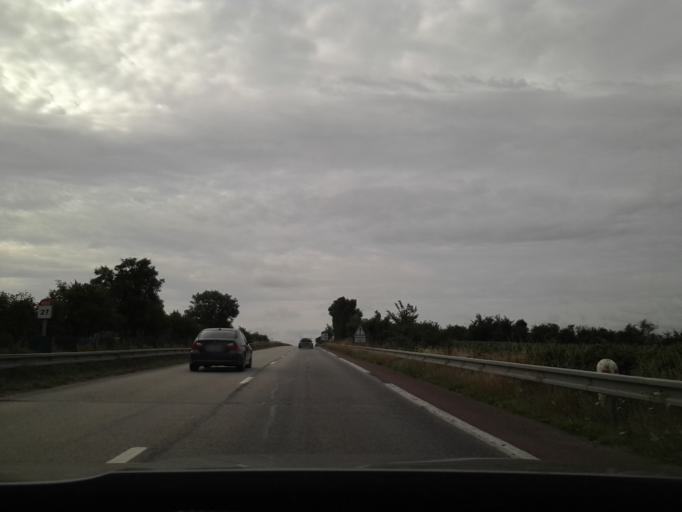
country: FR
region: Lower Normandy
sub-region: Departement de la Manche
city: Montebourg
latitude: 49.4576
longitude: -1.3555
